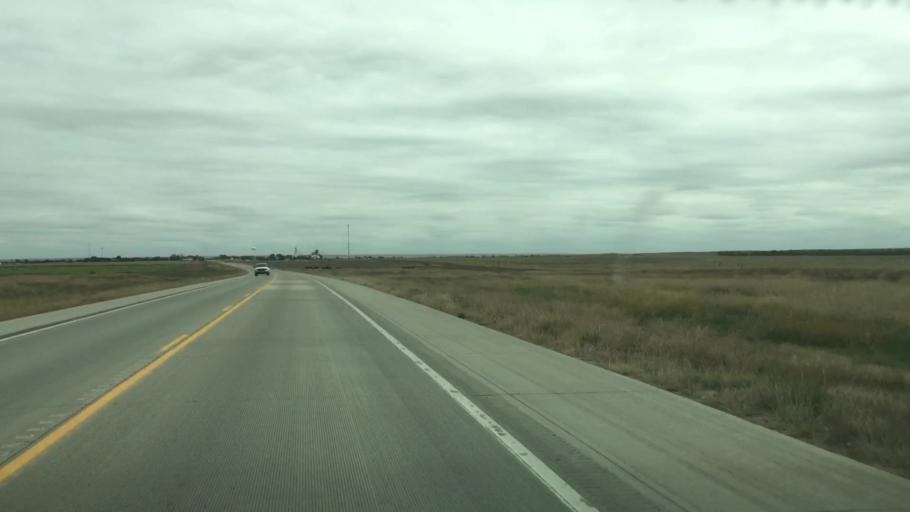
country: US
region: Colorado
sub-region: Kiowa County
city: Eads
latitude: 38.7639
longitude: -102.8245
